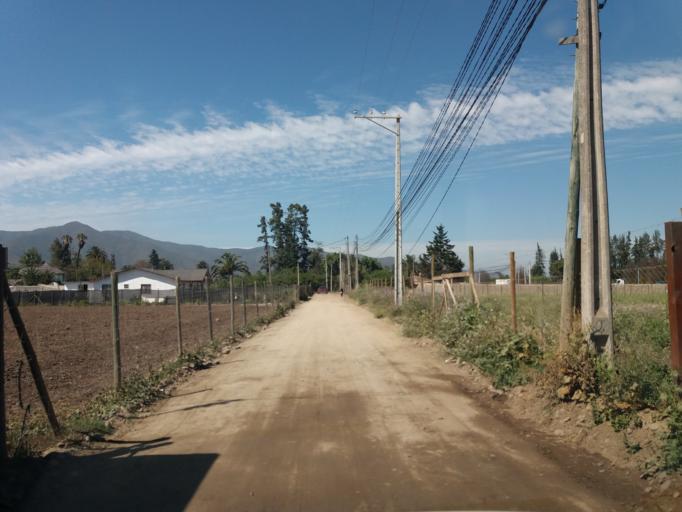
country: CL
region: Valparaiso
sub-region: Provincia de Quillota
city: Quillota
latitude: -32.8736
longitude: -71.2245
